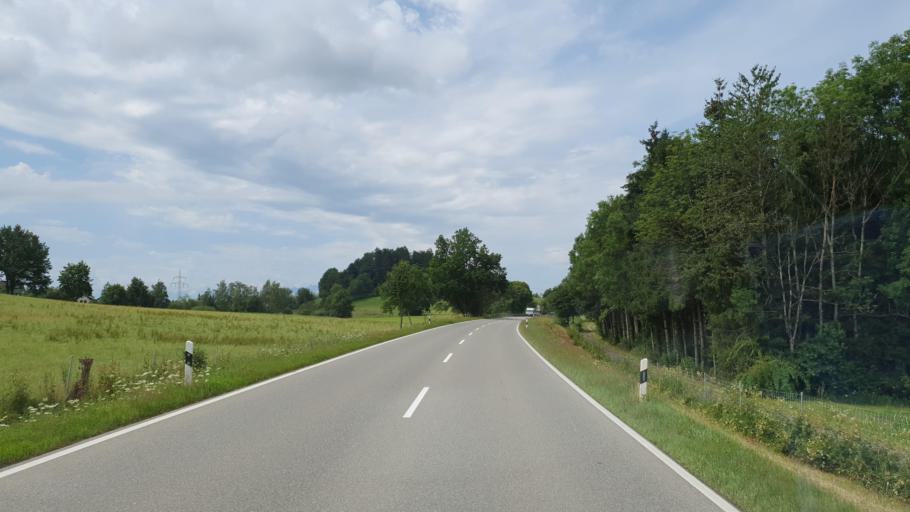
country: DE
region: Bavaria
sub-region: Swabia
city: Weissensberg
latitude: 47.5817
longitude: 9.7440
